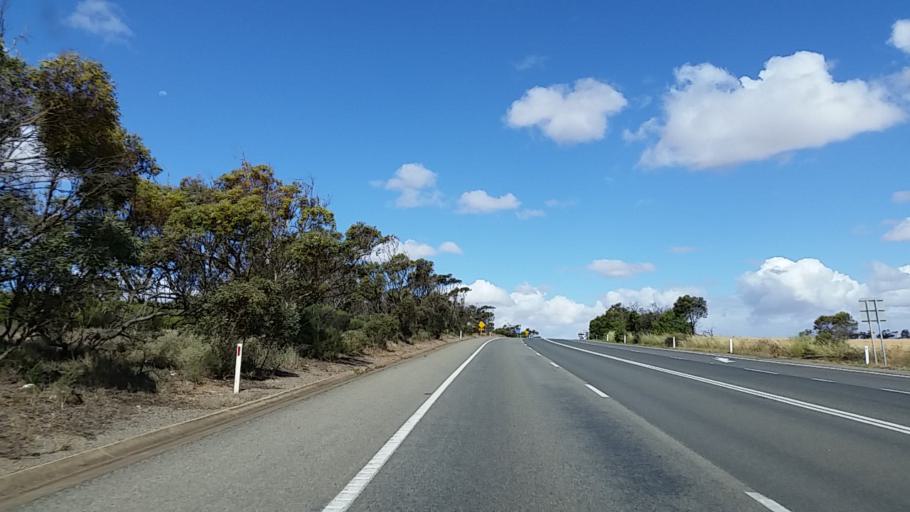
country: AU
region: South Australia
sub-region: Wakefield
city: Balaklava
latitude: -33.9707
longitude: 138.1914
